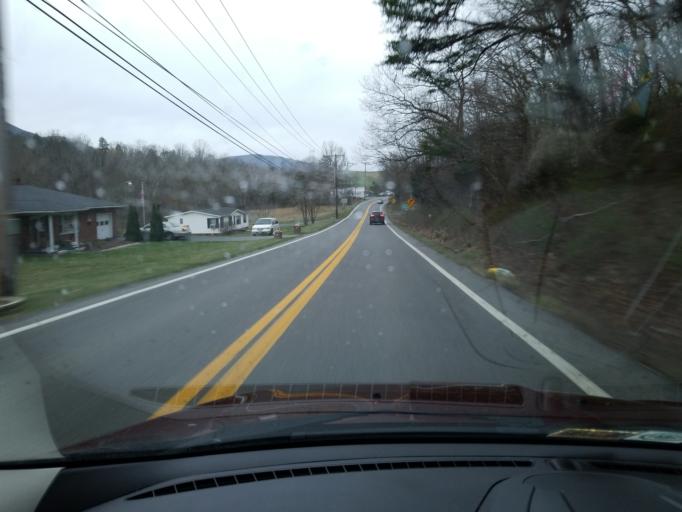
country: US
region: Virginia
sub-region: Giles County
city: Narrows
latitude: 37.3964
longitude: -80.7787
